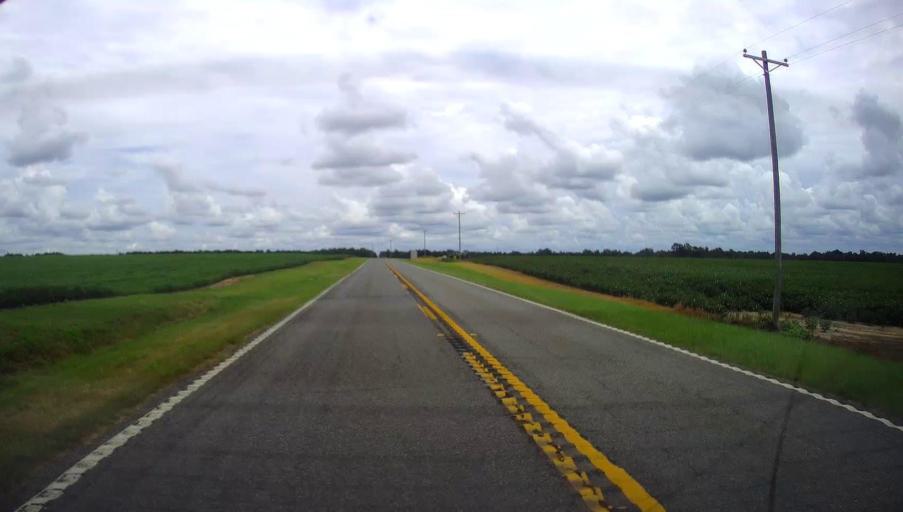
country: US
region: Georgia
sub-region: Dooly County
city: Unadilla
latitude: 32.2908
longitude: -83.8331
